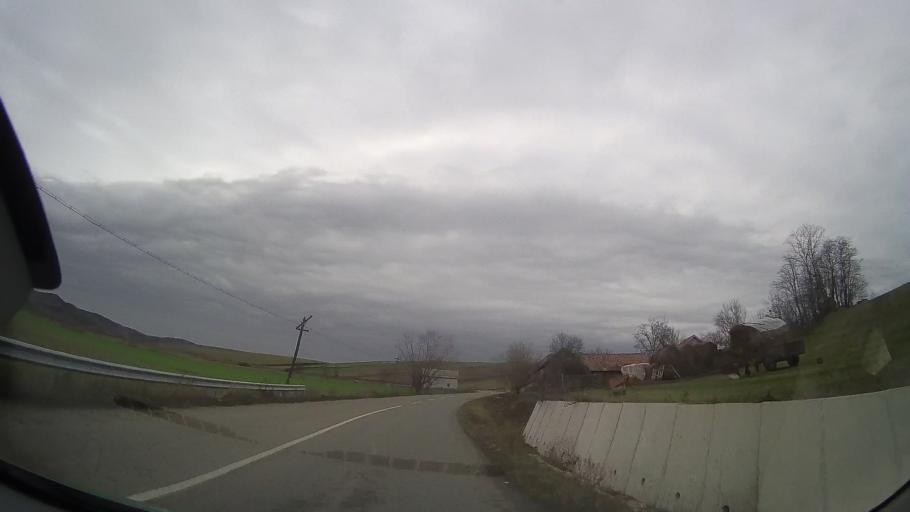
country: RO
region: Bistrita-Nasaud
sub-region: Comuna Milas
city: Milas
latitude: 46.7949
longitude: 24.4222
